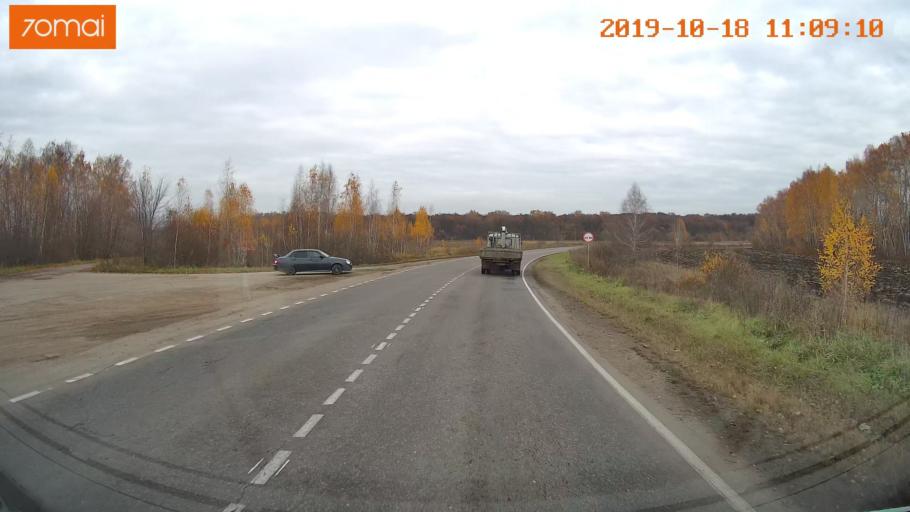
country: RU
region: Tula
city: Kimovsk
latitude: 53.9529
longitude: 38.5294
